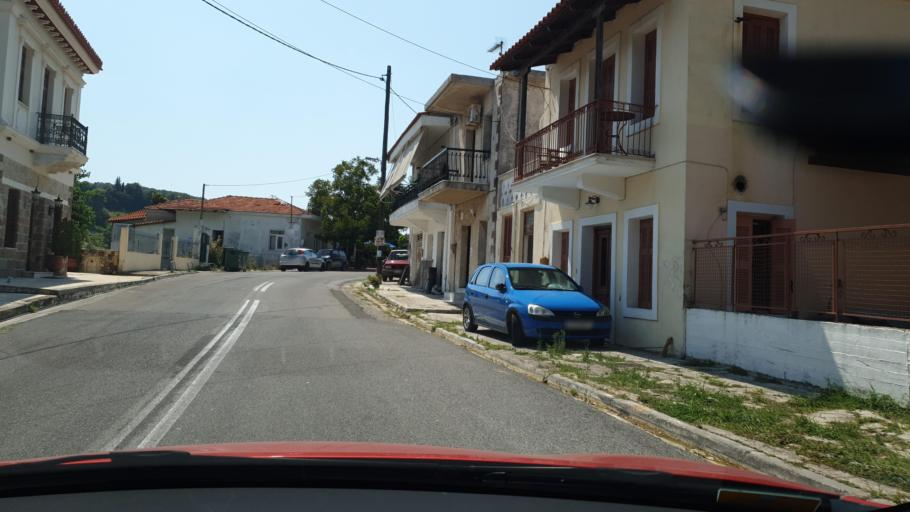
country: GR
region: Central Greece
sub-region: Nomos Evvoias
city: Oxilithos
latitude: 38.5899
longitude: 24.0692
